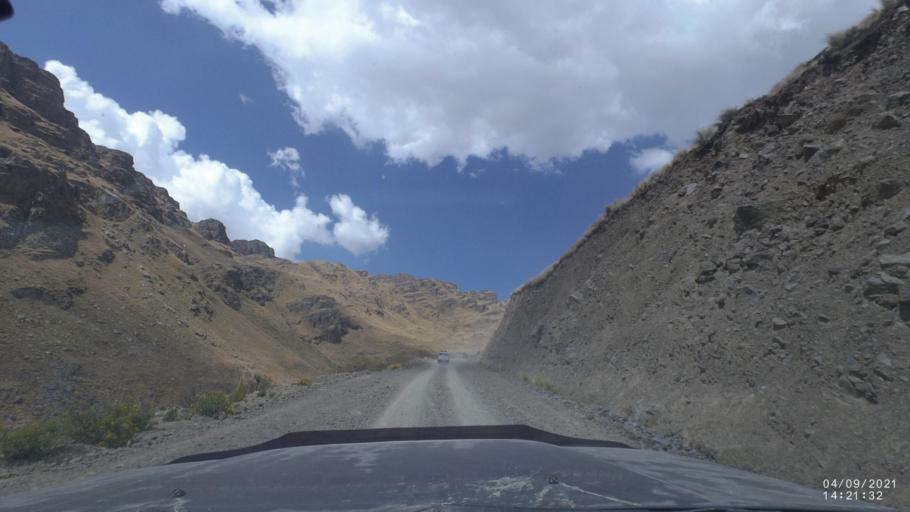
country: BO
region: Cochabamba
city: Sipe Sipe
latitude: -17.2364
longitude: -66.4160
